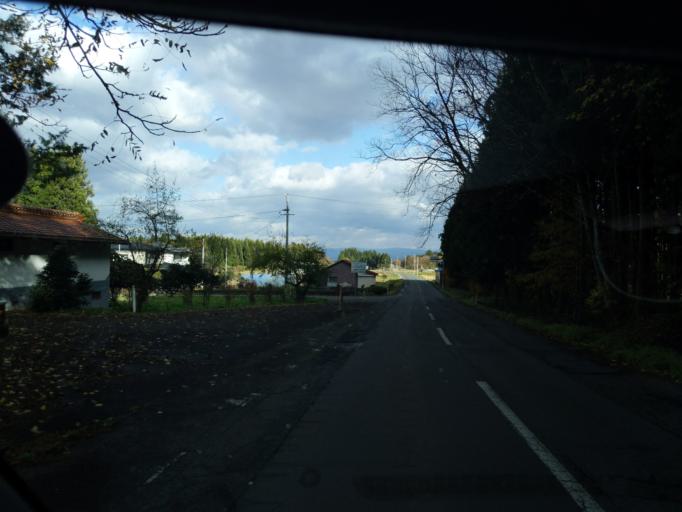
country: JP
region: Iwate
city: Mizusawa
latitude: 39.1155
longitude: 141.0377
